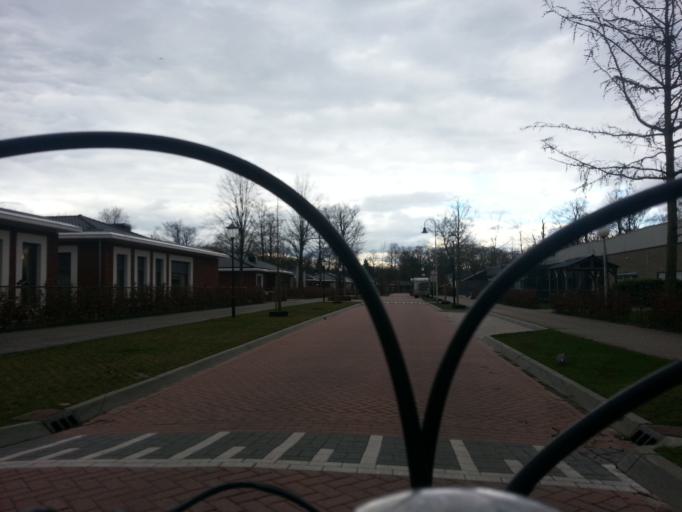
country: NL
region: North Brabant
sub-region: Gemeente Eindhoven
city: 't Hofke
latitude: 51.4629
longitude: 5.5024
